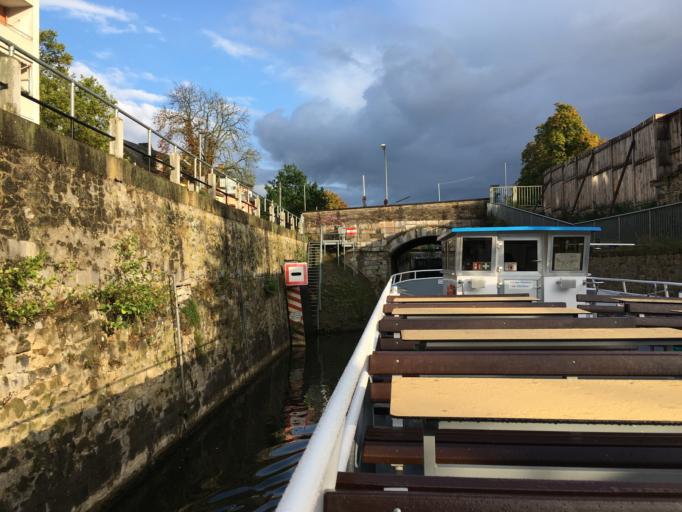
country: DE
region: Hesse
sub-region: Regierungsbezirk Giessen
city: Limburg an der Lahn
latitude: 50.3916
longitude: 8.0648
